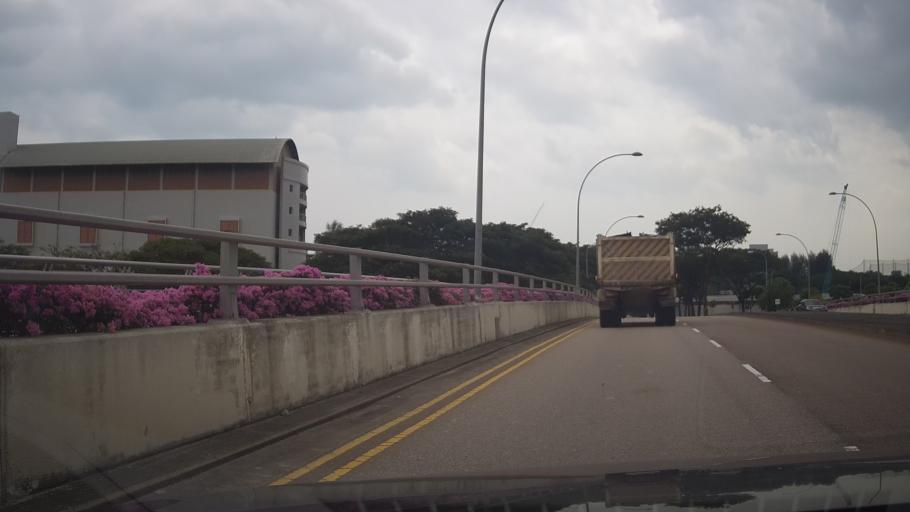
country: SG
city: Singapore
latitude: 1.2990
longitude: 103.8776
